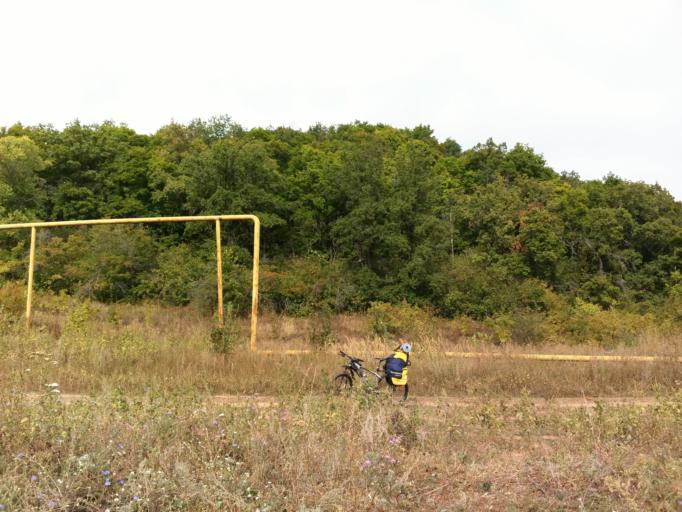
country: RU
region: Samara
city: Novokuybyshevsk
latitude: 53.2418
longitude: 49.8248
